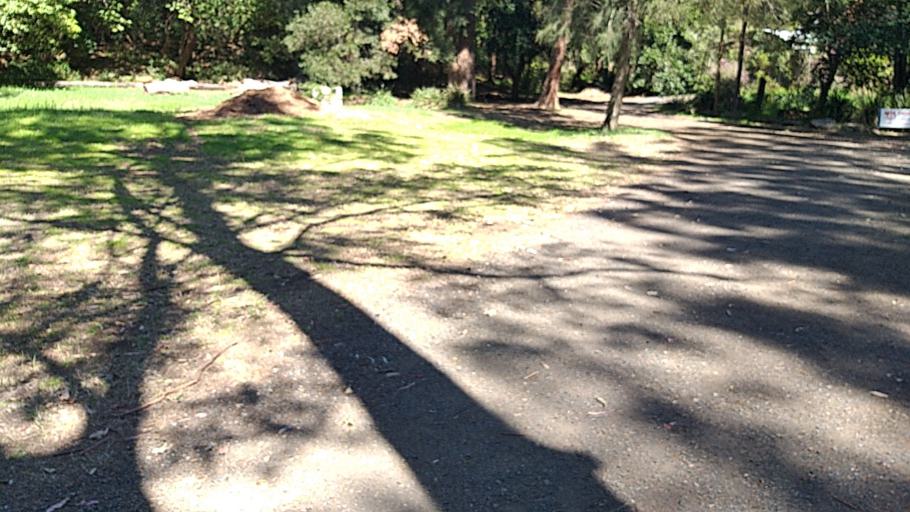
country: AU
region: New South Wales
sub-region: Ryde
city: East Ryde
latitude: -33.8159
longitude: 151.1334
